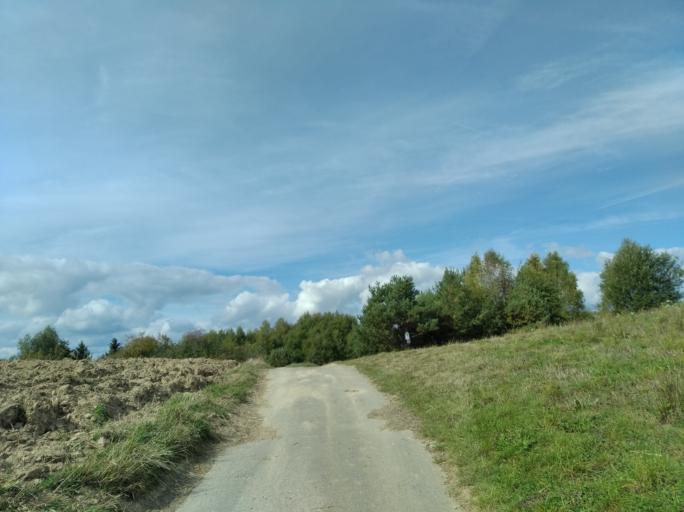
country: PL
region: Subcarpathian Voivodeship
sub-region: Powiat strzyzowski
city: Jawornik
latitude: 49.8425
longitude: 21.8662
